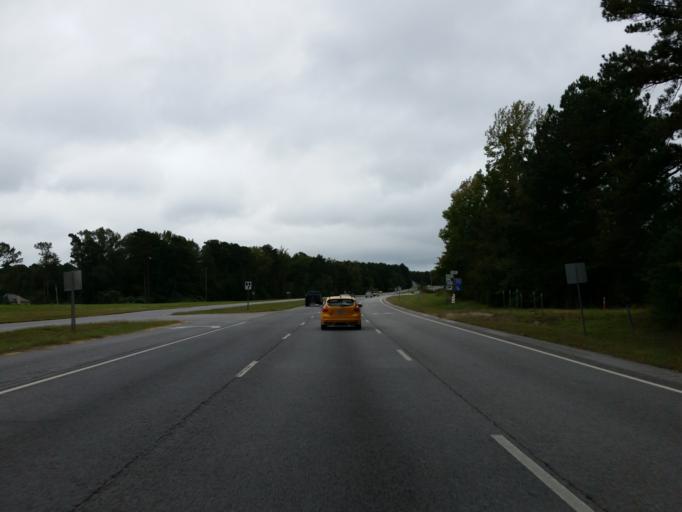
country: US
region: Georgia
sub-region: Henry County
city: Hampton
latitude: 33.3740
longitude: -84.2974
